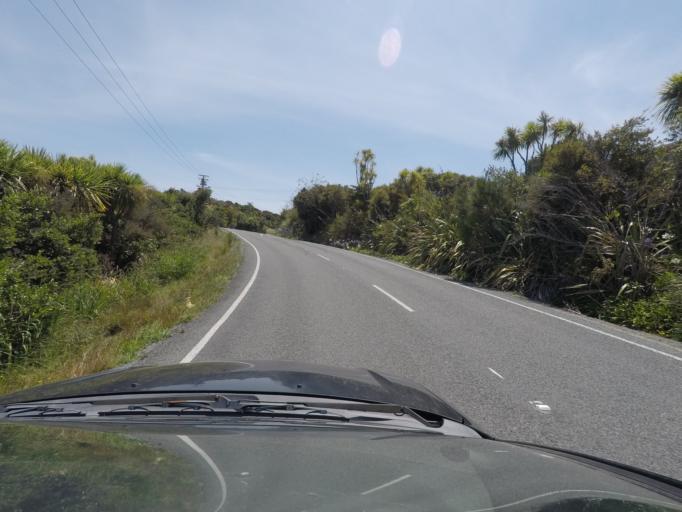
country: NZ
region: Auckland
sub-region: Auckland
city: Warkworth
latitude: -36.3017
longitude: 174.7920
